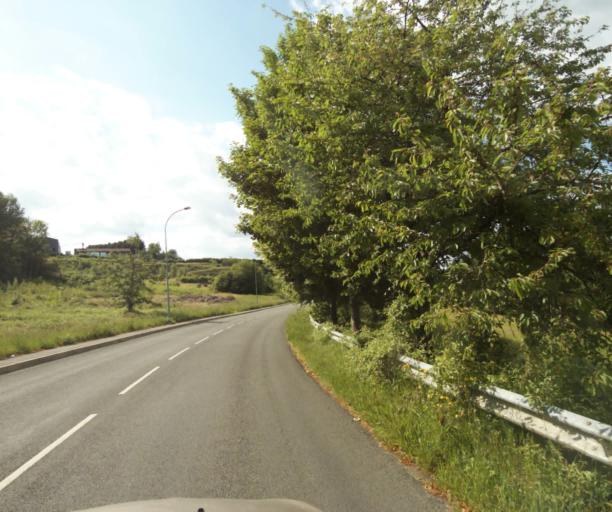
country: FR
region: Champagne-Ardenne
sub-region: Departement des Ardennes
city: Montcy-Notre-Dame
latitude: 49.7628
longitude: 4.7447
